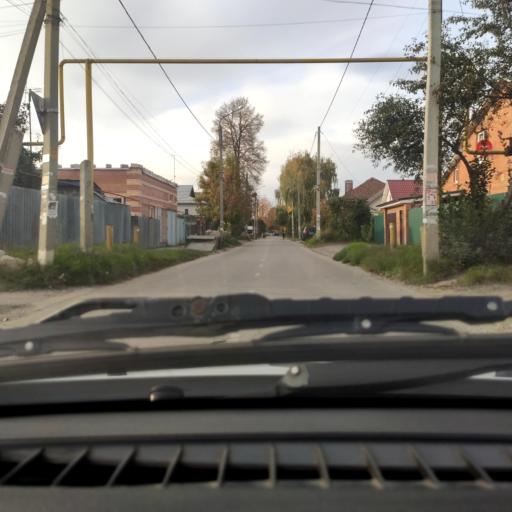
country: RU
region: Samara
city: Tol'yatti
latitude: 53.5219
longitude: 49.4084
